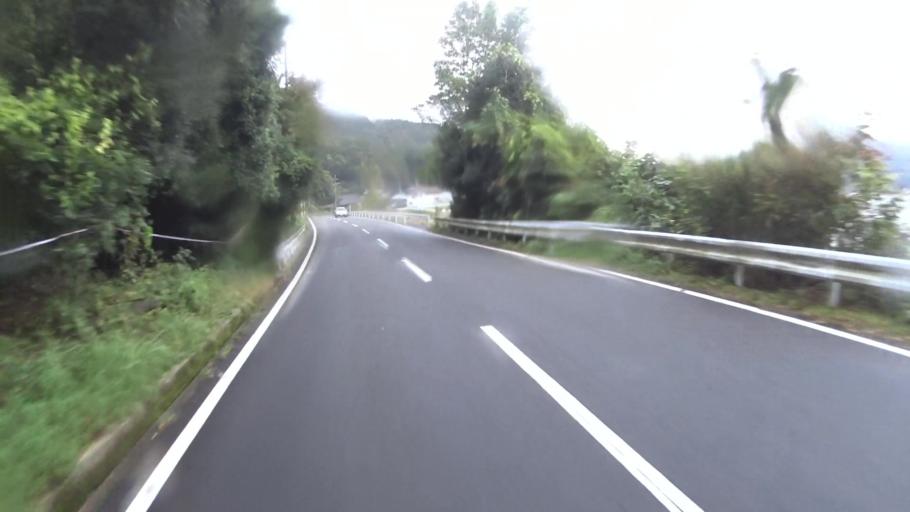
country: JP
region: Kyoto
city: Miyazu
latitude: 35.5596
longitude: 135.2408
